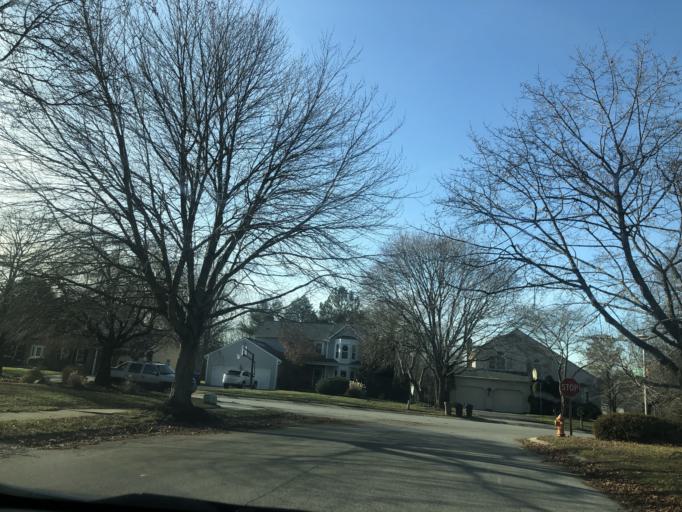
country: US
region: Maryland
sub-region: Howard County
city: Columbia
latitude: 39.2800
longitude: -76.8473
